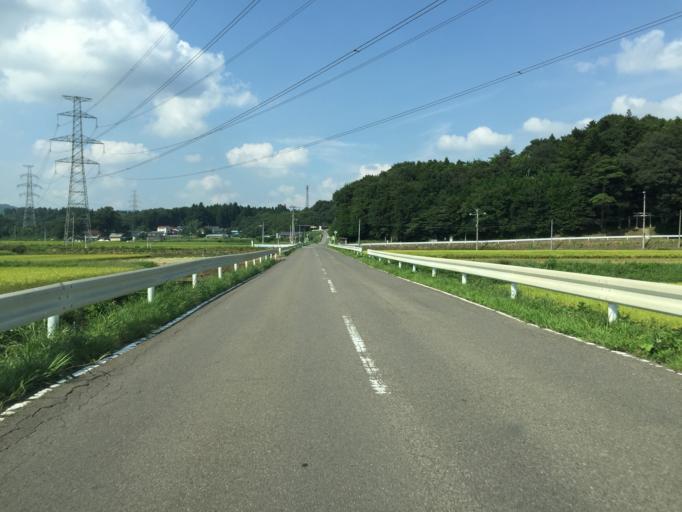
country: JP
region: Fukushima
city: Nihommatsu
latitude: 37.5658
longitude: 140.3843
